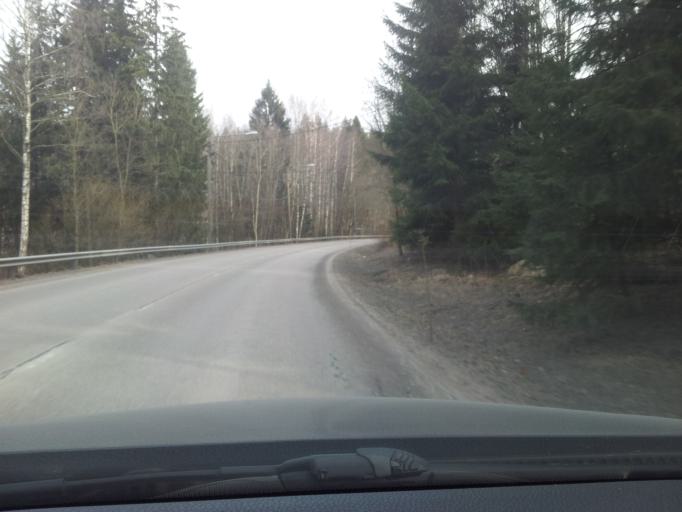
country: FI
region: Uusimaa
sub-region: Helsinki
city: Koukkuniemi
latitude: 60.1844
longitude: 24.7537
